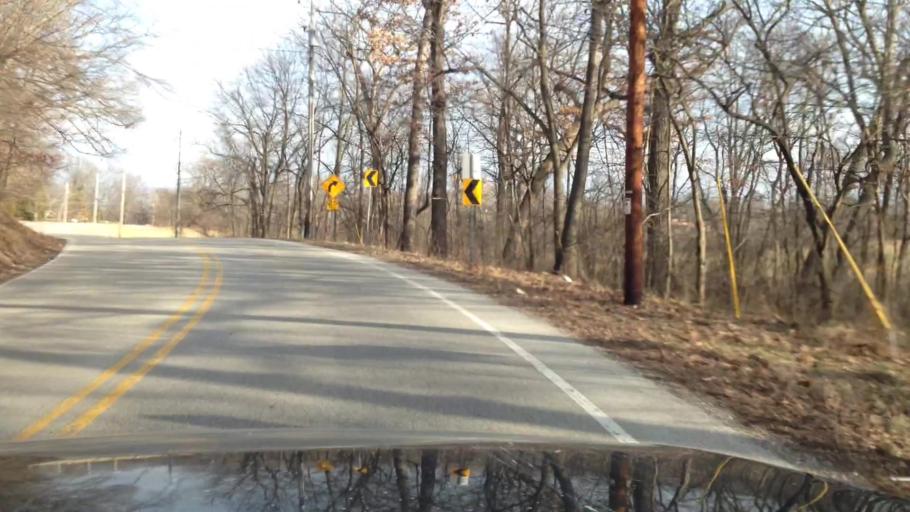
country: US
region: Wisconsin
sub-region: Waukesha County
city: Muskego
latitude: 42.9292
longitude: -88.1288
